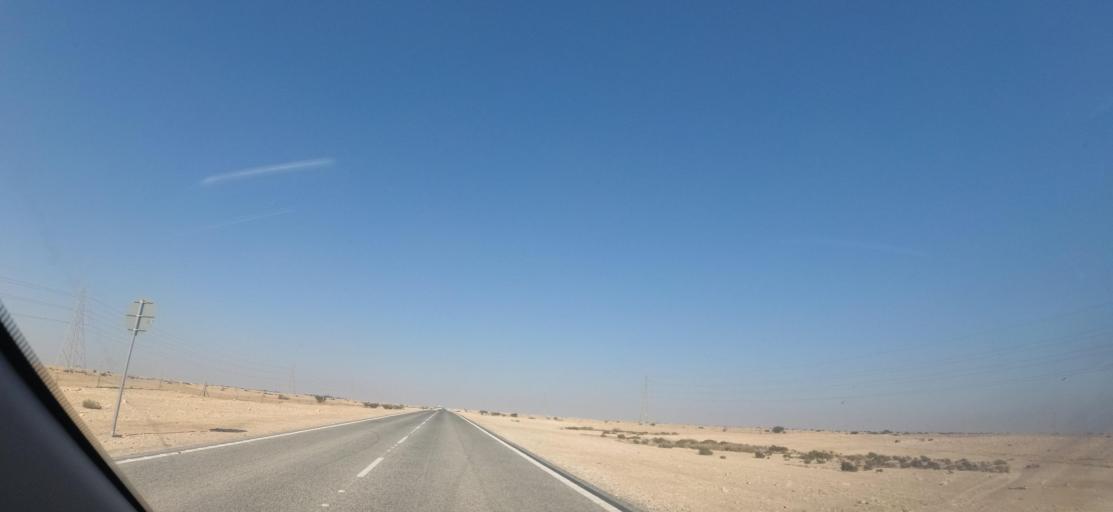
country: QA
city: Al Jumayliyah
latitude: 25.6495
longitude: 51.1108
